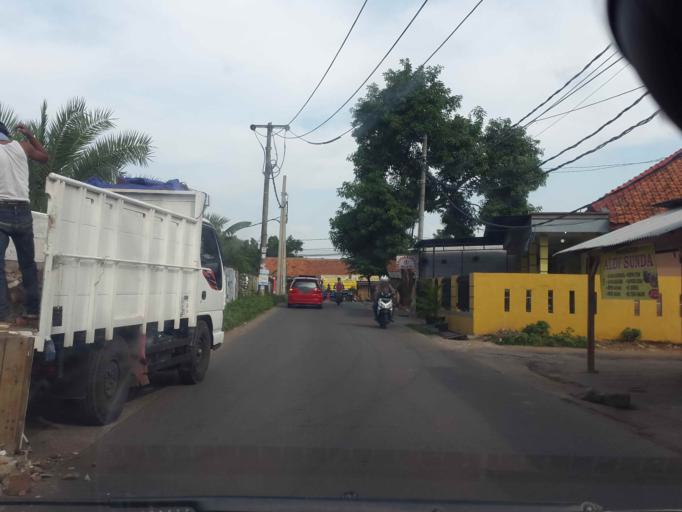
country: ID
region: West Java
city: Ciputat
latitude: -6.2582
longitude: 106.6683
